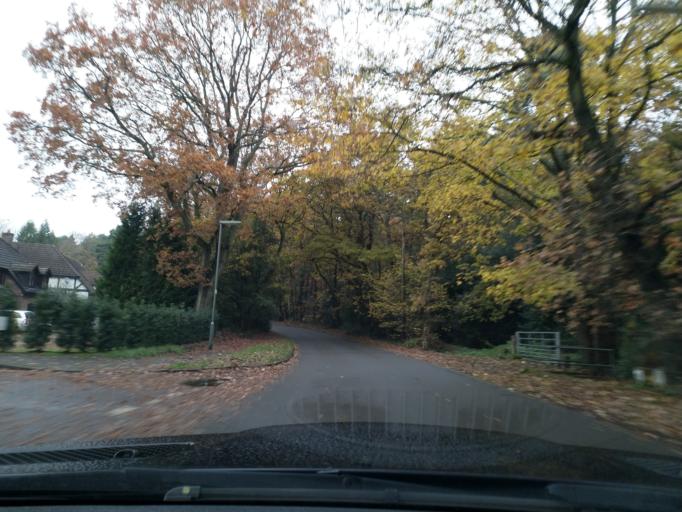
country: GB
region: England
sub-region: Surrey
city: Frimley
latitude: 51.3105
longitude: -0.7193
